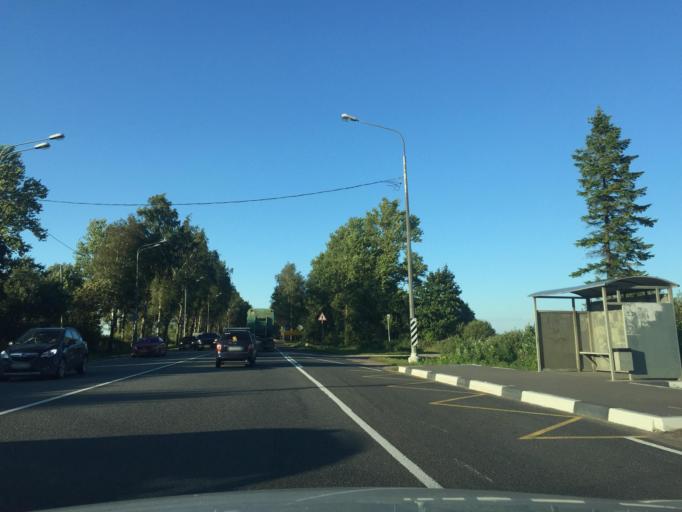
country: RU
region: Leningrad
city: Voyskovitsy
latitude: 59.4693
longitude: 30.0079
